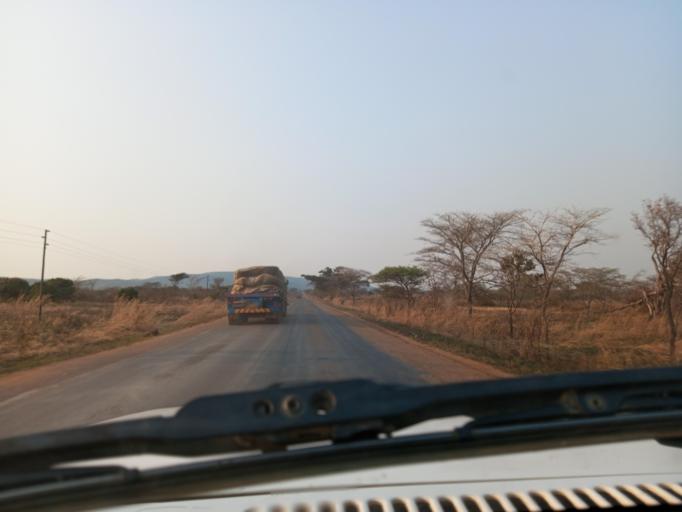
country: ZM
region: Northern
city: Mpika
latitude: -11.9287
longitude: 31.4181
